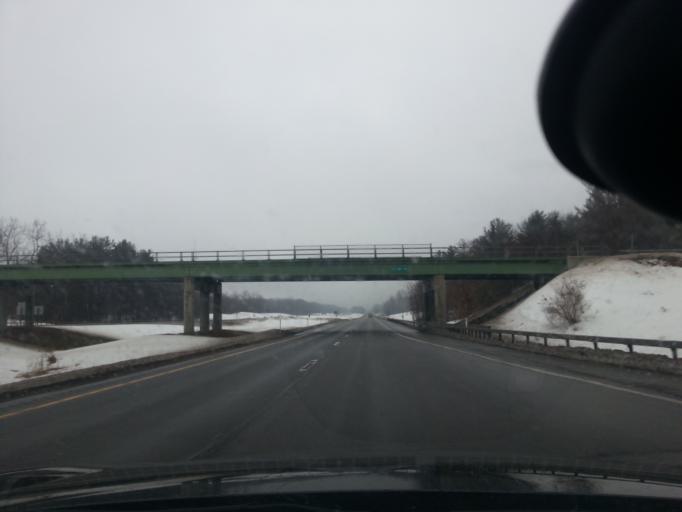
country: US
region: New York
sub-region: Jefferson County
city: Adams
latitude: 43.7115
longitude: -76.0761
